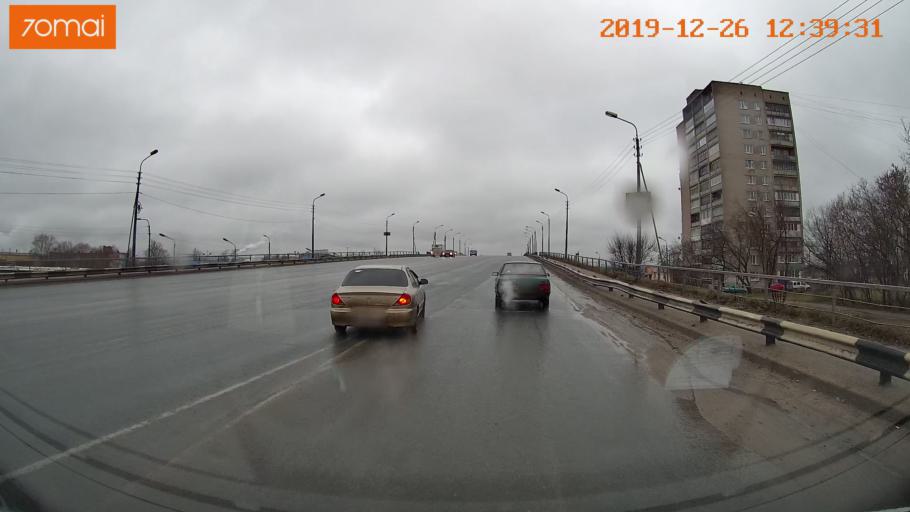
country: RU
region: Vologda
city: Tonshalovo
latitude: 59.1344
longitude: 37.9786
